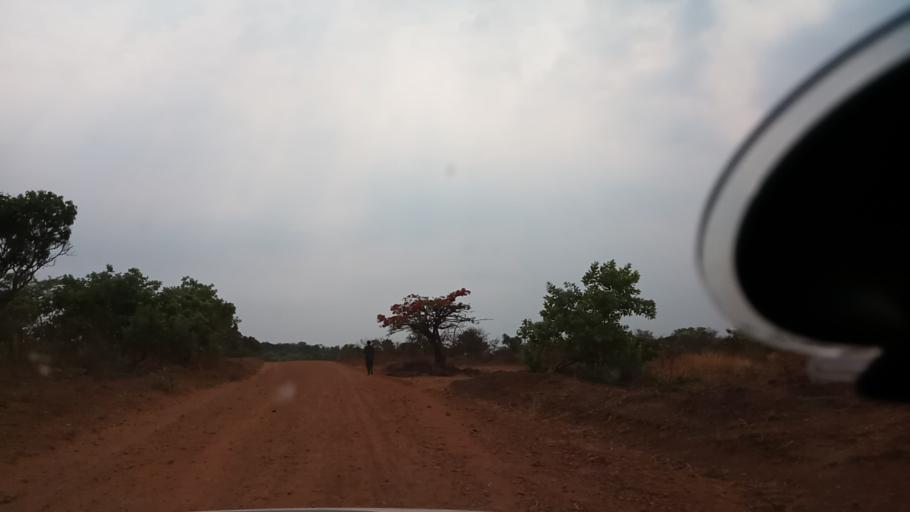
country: ZM
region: Luapula
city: Nchelenge
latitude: -9.0985
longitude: 28.3099
